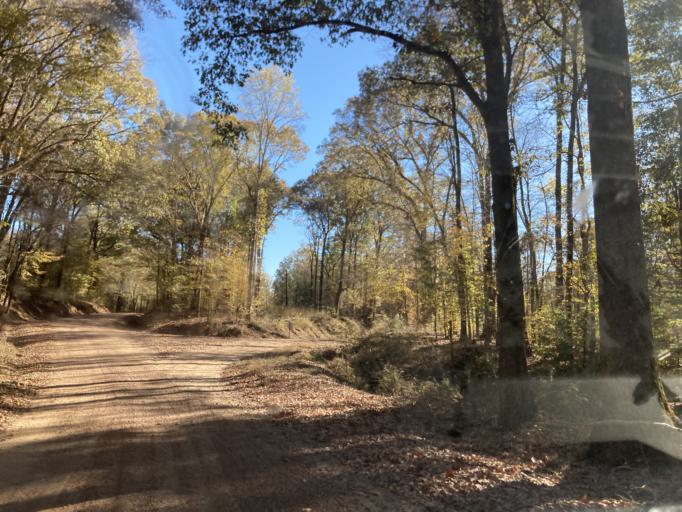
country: US
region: Mississippi
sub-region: Yazoo County
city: Yazoo City
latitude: 32.7539
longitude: -90.3897
